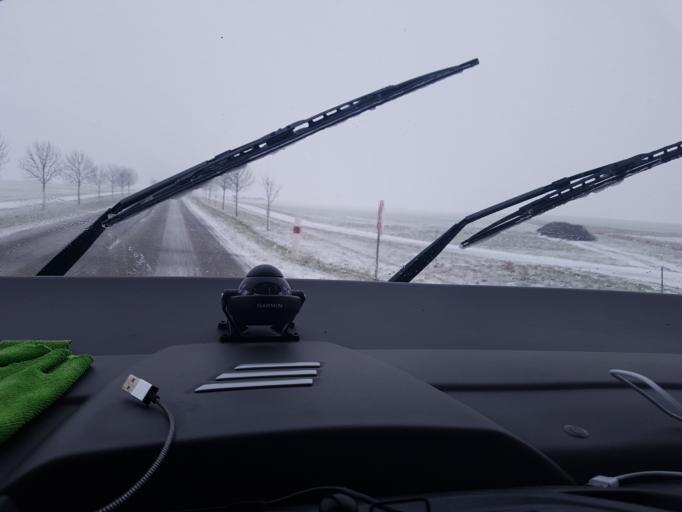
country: FR
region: Lorraine
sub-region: Departement de la Moselle
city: Chateau-Salins
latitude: 48.8615
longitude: 6.4377
